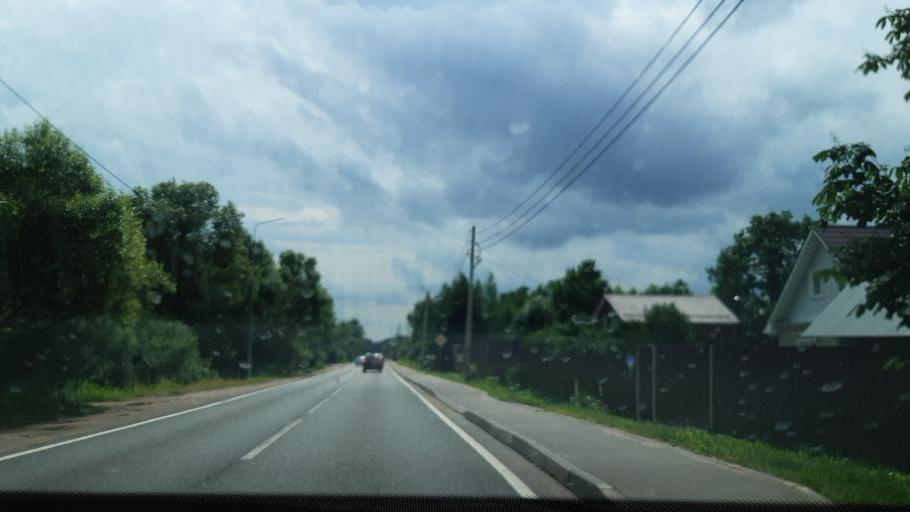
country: RU
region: Moskovskaya
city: Dorokhovo
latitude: 55.5348
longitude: 36.3621
